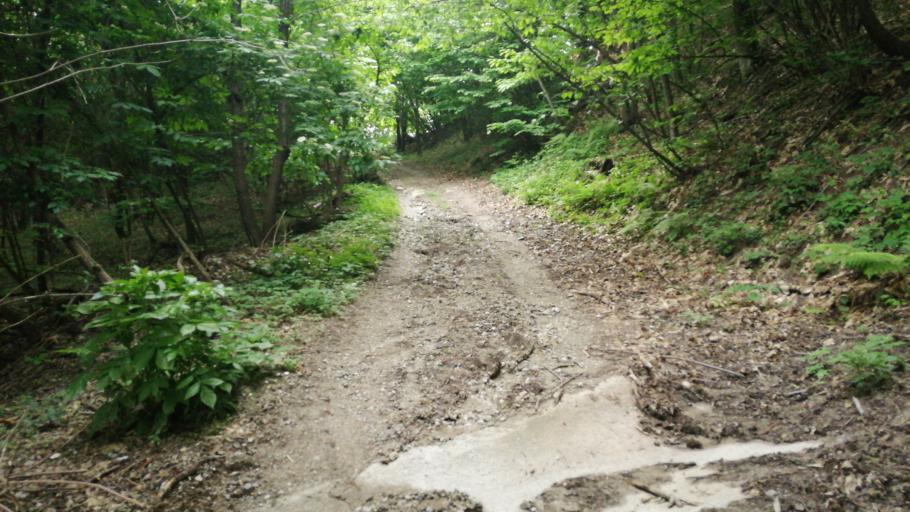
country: IT
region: Piedmont
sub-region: Provincia di Cuneo
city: Montaldo di Mondovi
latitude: 44.3148
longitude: 7.8630
